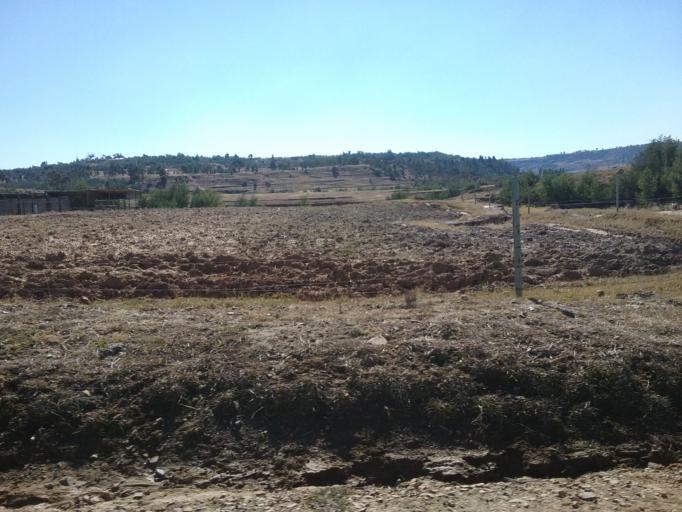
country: LS
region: Maseru
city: Maseru
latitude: -29.4438
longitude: 27.5736
